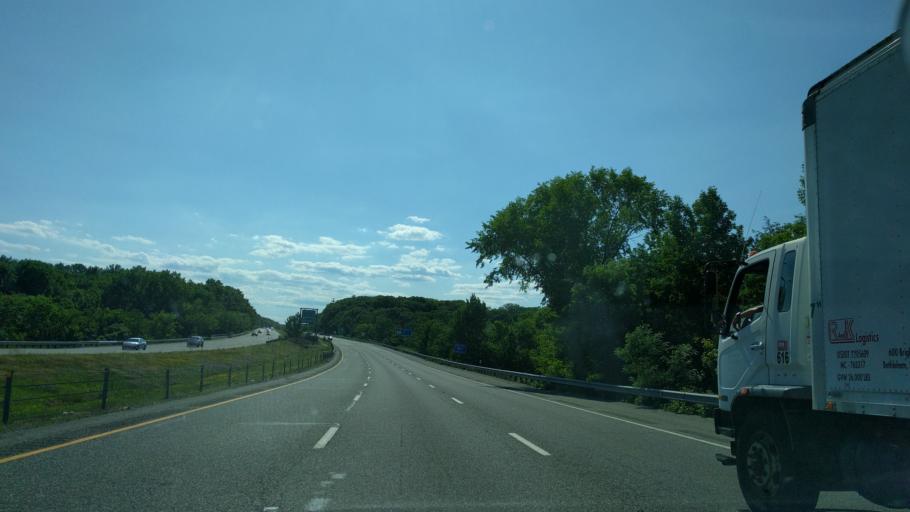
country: US
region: Rhode Island
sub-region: Providence County
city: Valley Falls
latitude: 41.9532
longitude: -71.3850
